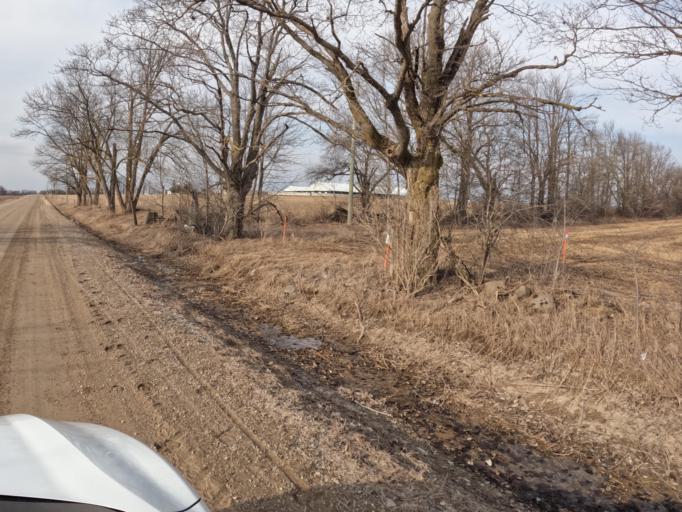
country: CA
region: Ontario
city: Orangeville
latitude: 43.9001
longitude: -80.2678
